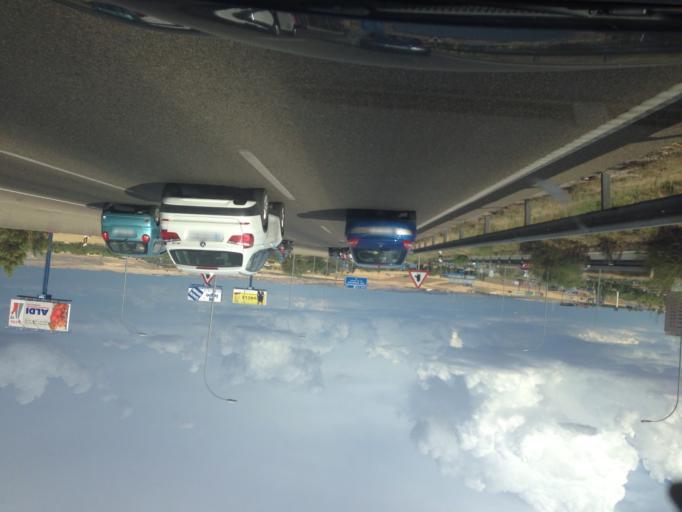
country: ES
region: Madrid
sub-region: Provincia de Madrid
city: San Sebastian de los Reyes
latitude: 40.5335
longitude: -3.6164
